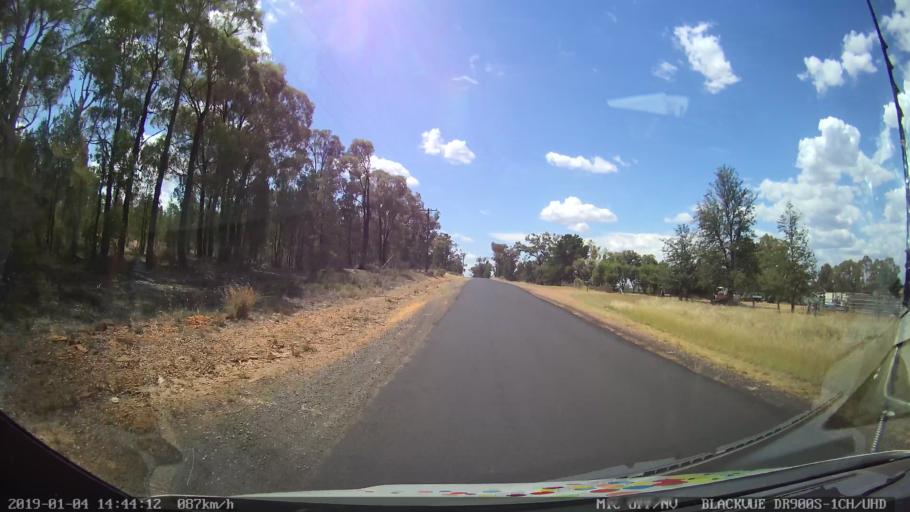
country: AU
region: New South Wales
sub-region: Dubbo Municipality
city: Dubbo
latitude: -32.1093
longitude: 148.6551
